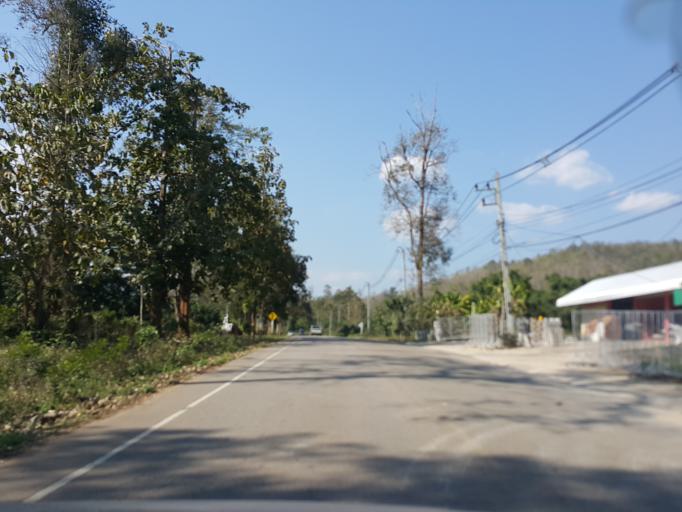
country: TH
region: Chiang Mai
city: Mae Wang
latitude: 18.6426
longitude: 98.6995
